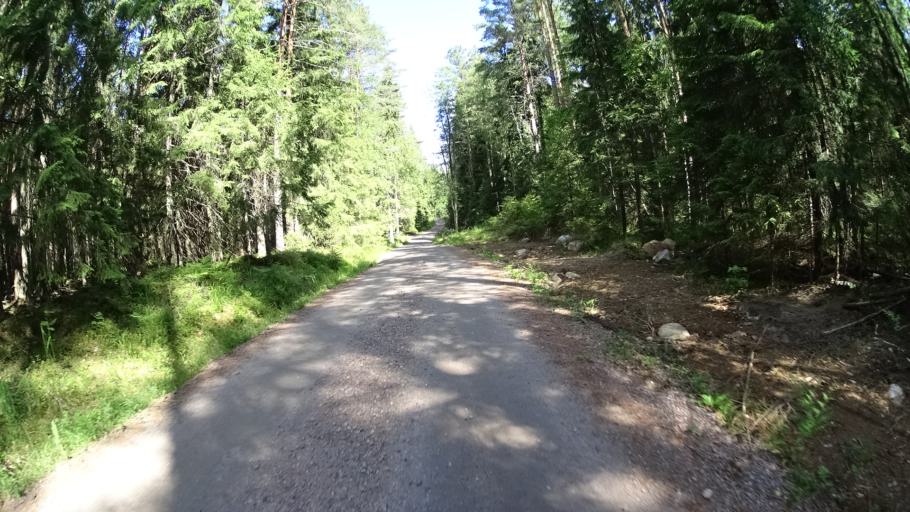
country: FI
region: Uusimaa
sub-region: Helsinki
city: Vihti
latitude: 60.3157
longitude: 24.4467
